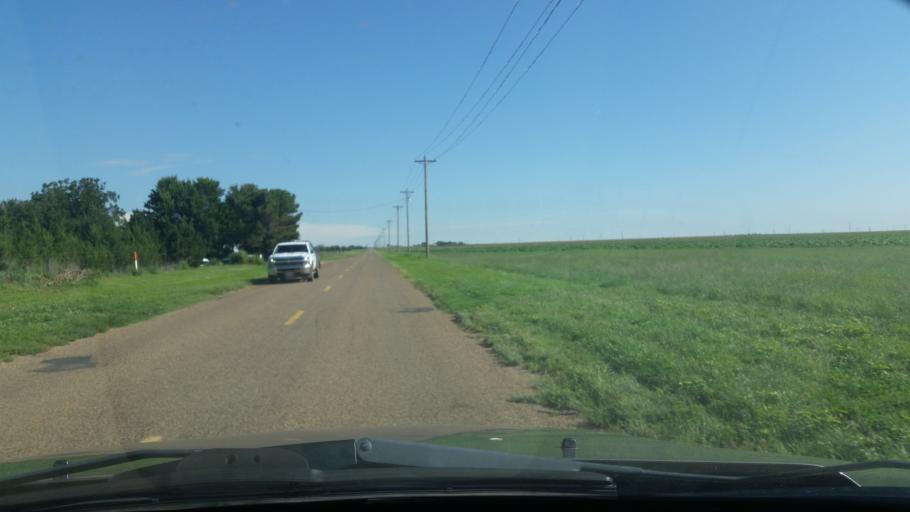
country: US
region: New Mexico
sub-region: Curry County
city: Clovis
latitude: 34.4354
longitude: -103.1608
